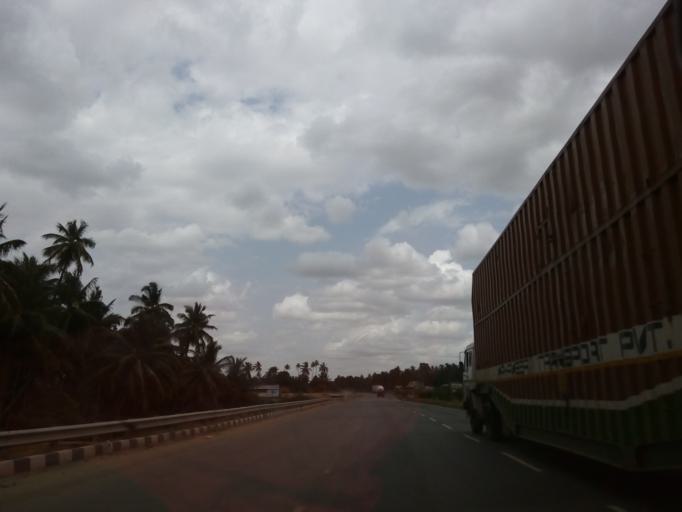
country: IN
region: Karnataka
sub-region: Chitradurga
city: Hiriyur
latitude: 13.9264
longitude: 76.6333
